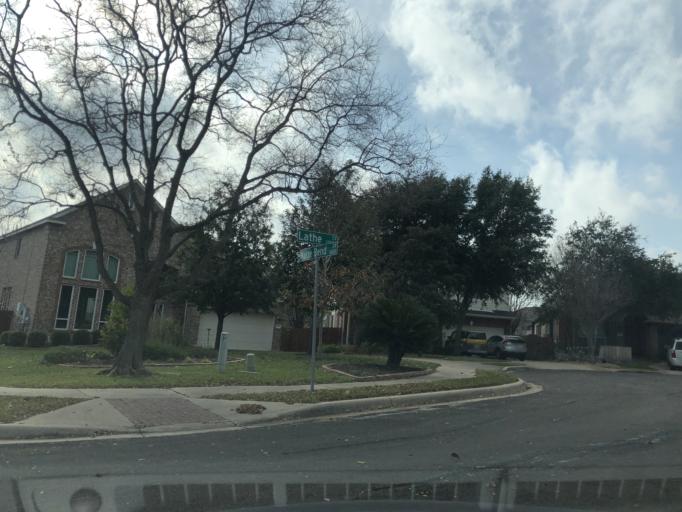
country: US
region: Texas
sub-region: Travis County
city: Wells Branch
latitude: 30.4257
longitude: -97.6806
